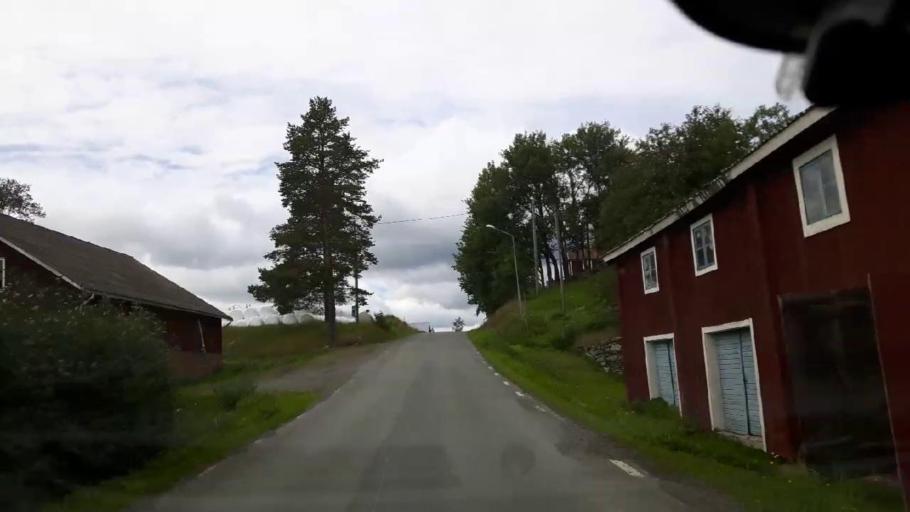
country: SE
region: Jaemtland
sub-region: Krokoms Kommun
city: Valla
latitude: 63.4833
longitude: 14.0501
